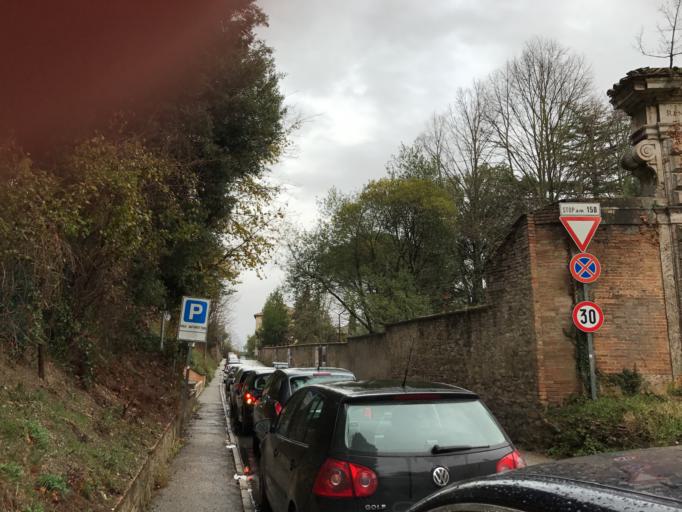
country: IT
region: Umbria
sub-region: Provincia di Perugia
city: Perugia
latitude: 43.1127
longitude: 12.4009
